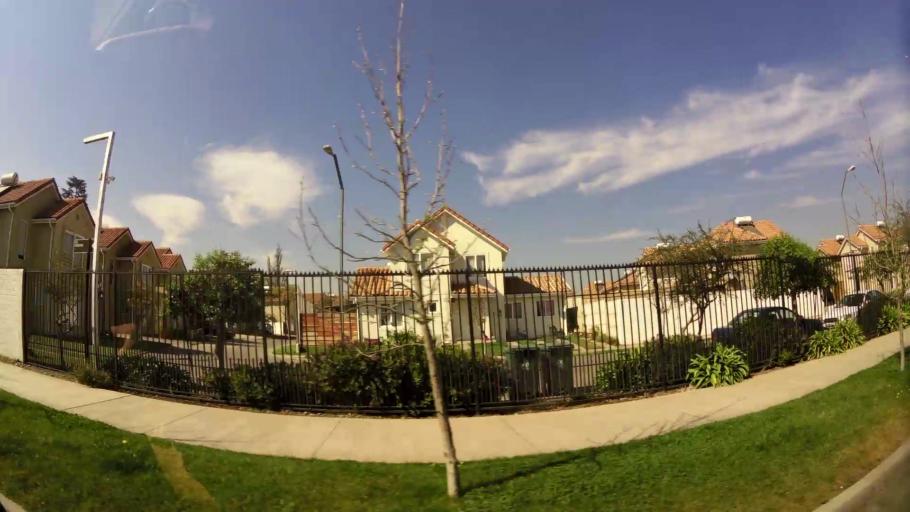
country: CL
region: Santiago Metropolitan
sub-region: Provincia de Talagante
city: Penaflor
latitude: -33.5717
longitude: -70.8241
